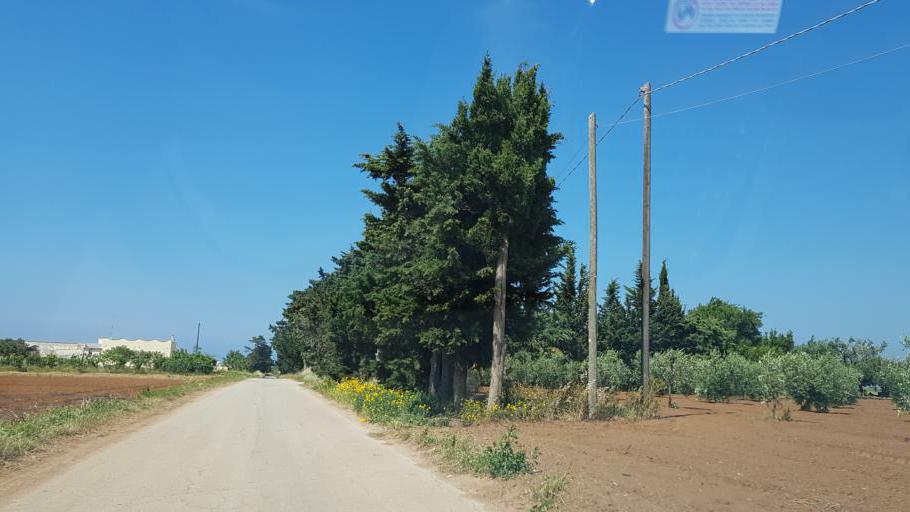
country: IT
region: Apulia
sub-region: Provincia di Brindisi
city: Brindisi
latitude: 40.6649
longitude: 17.8613
